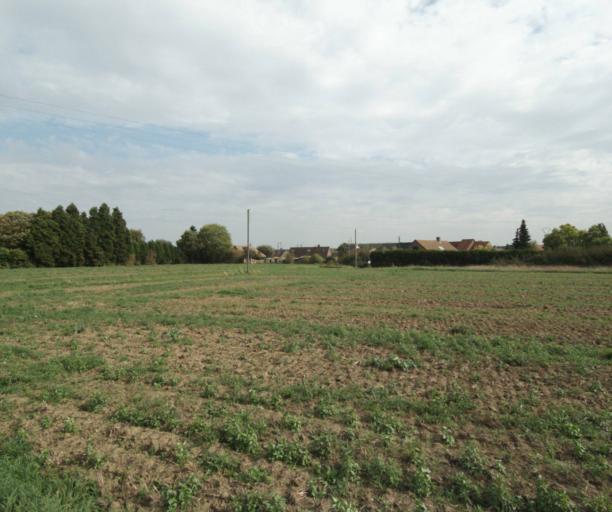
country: FR
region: Nord-Pas-de-Calais
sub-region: Departement du Nord
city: Marquillies
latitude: 50.5395
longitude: 2.8727
